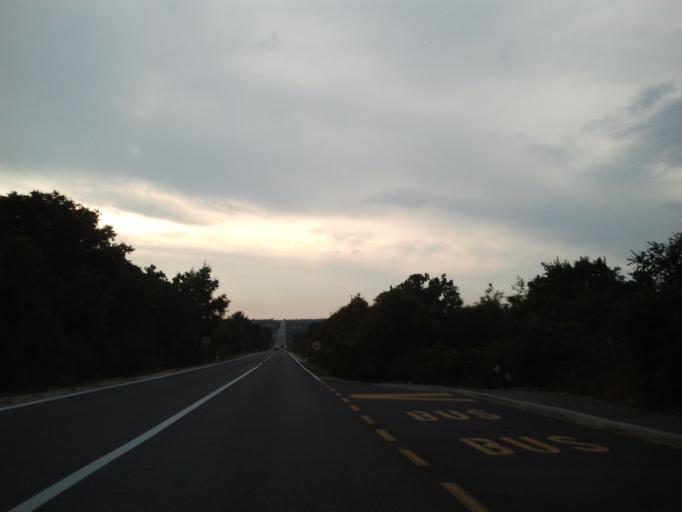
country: HR
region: Zadarska
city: Posedarje
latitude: 44.2268
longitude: 15.4328
